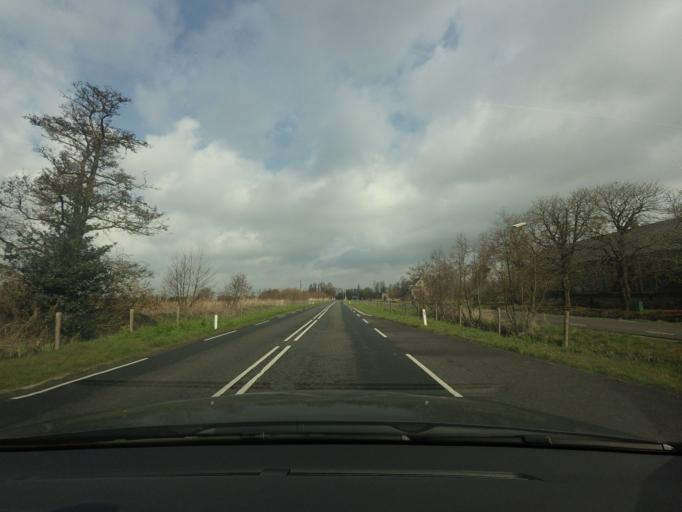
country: NL
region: Utrecht
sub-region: Gemeente De Ronde Venen
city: Mijdrecht
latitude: 52.1625
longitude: 4.8546
